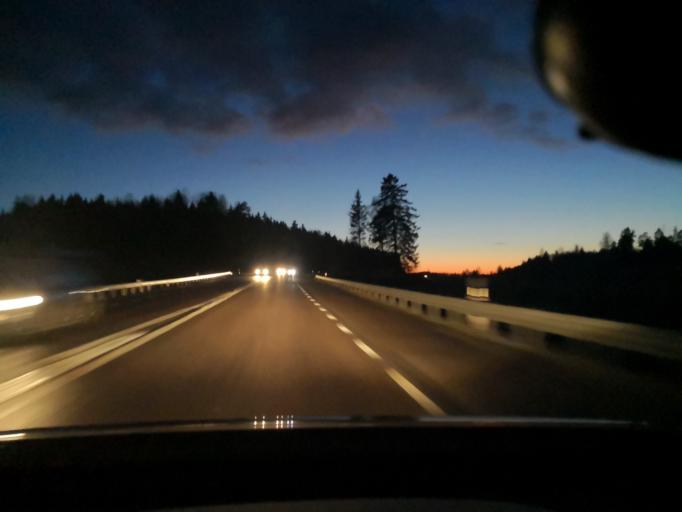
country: SE
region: Vaestmanland
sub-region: Sala Kommun
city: Sala
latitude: 59.9320
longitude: 16.7288
